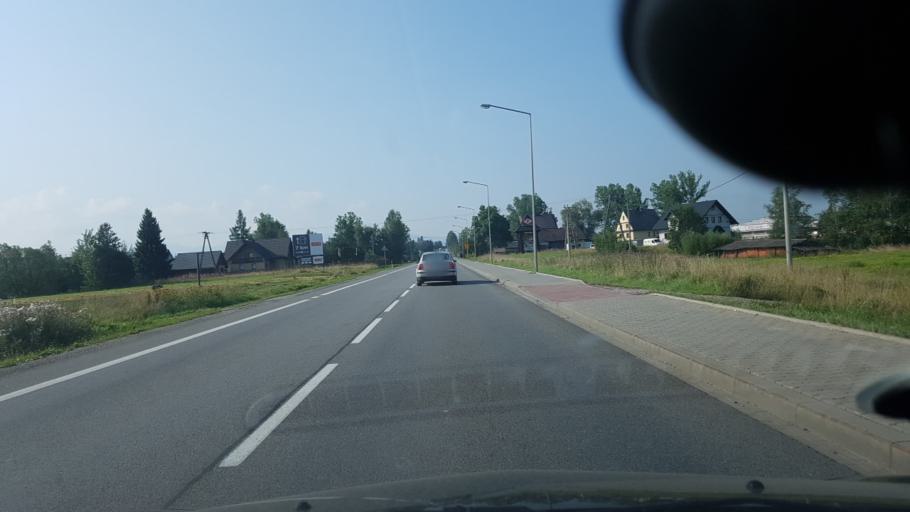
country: PL
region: Lesser Poland Voivodeship
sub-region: Powiat nowotarski
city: Jablonka
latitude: 49.4671
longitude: 19.6917
